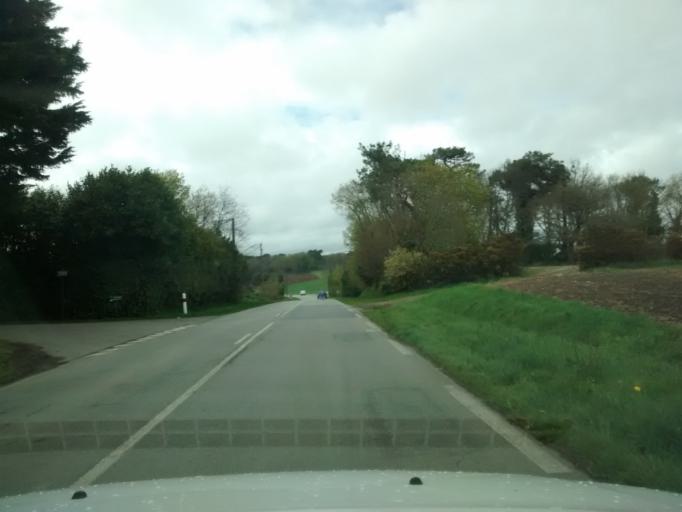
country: FR
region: Brittany
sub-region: Departement du Morbihan
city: Gestel
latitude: 47.7885
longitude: -3.4541
